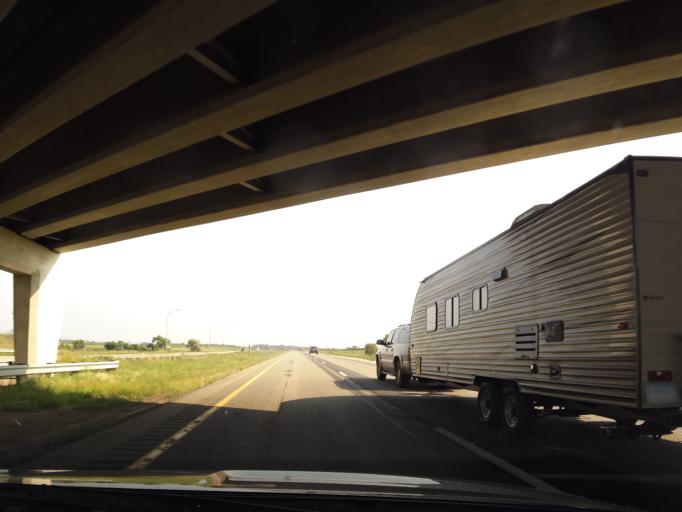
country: US
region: Minnesota
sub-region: Douglas County
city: Alexandria
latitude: 45.8604
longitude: -95.4301
